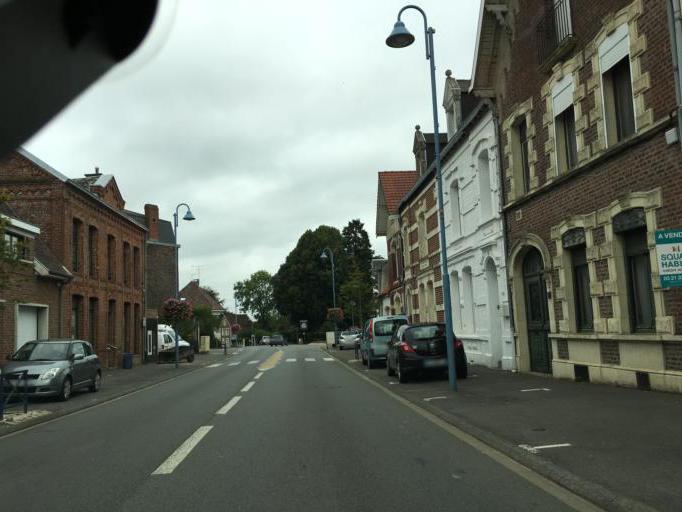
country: FR
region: Nord-Pas-de-Calais
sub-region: Departement du Pas-de-Calais
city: Saint-Pol-sur-Ternoise
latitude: 50.3775
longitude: 2.3332
